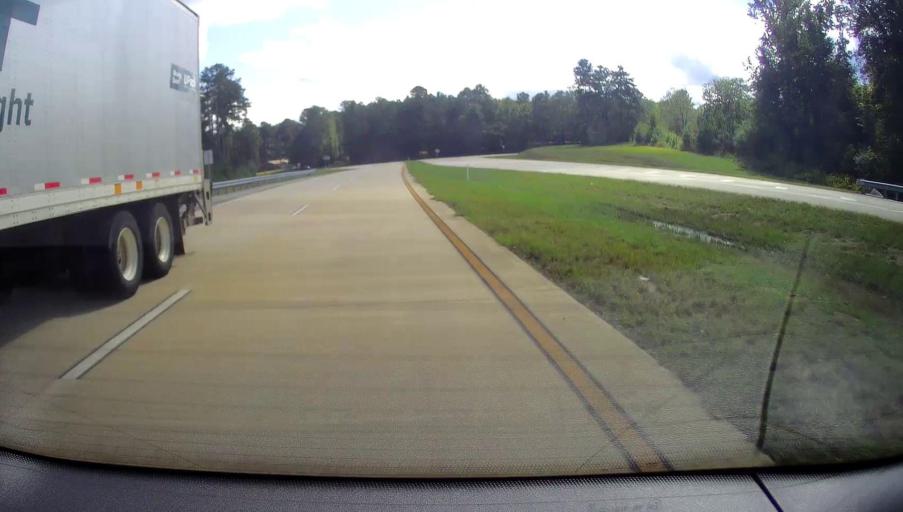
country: US
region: Georgia
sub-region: Jones County
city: Gray
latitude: 33.0186
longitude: -83.5130
